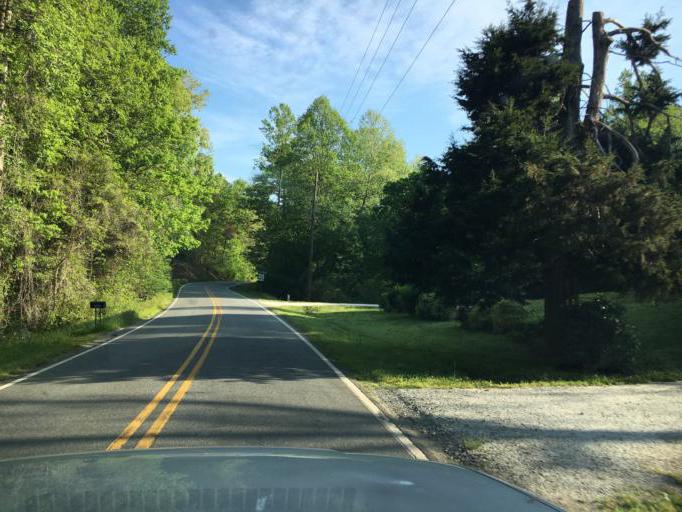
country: US
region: North Carolina
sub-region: Rutherford County
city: Rutherfordton
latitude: 35.2999
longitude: -82.0056
